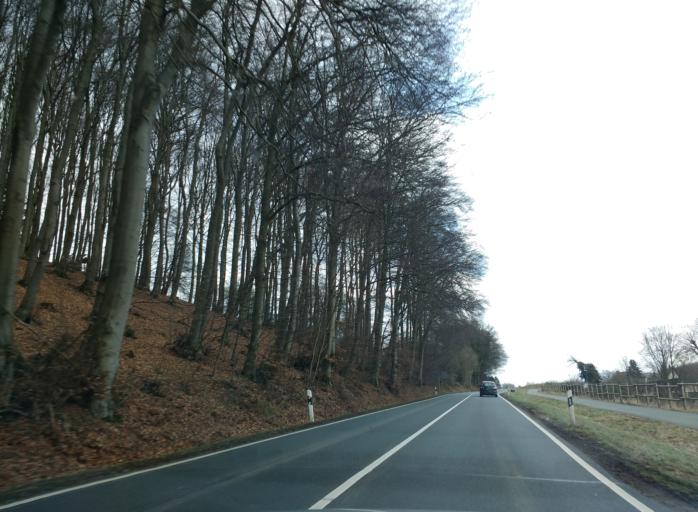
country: DE
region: North Rhine-Westphalia
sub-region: Regierungsbezirk Detmold
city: Lemgo
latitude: 52.0840
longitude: 8.9326
